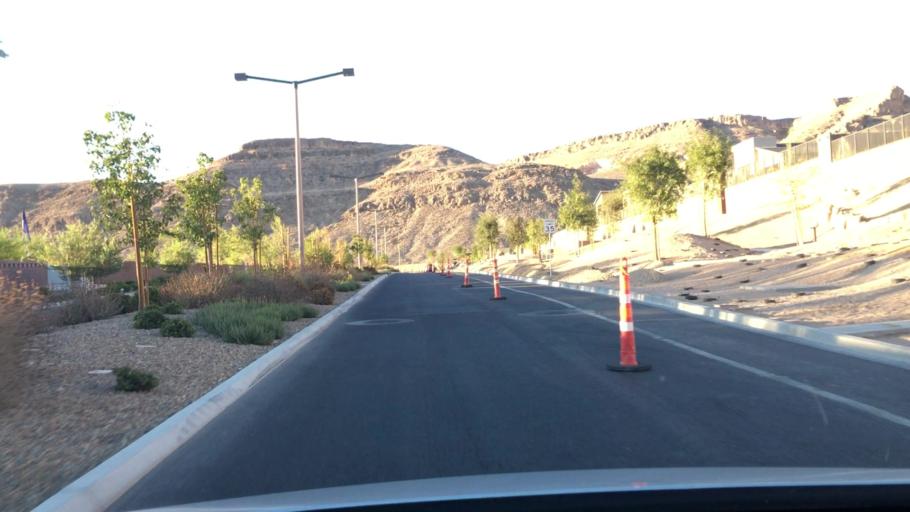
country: US
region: Nevada
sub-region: Clark County
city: Summerlin South
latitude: 36.0661
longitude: -115.3158
